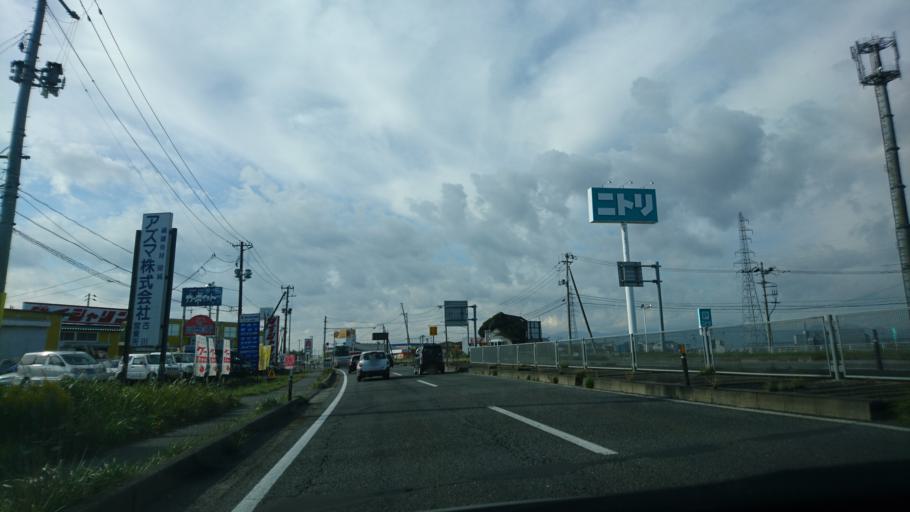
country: JP
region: Miyagi
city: Furukawa
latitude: 38.5830
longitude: 140.9470
